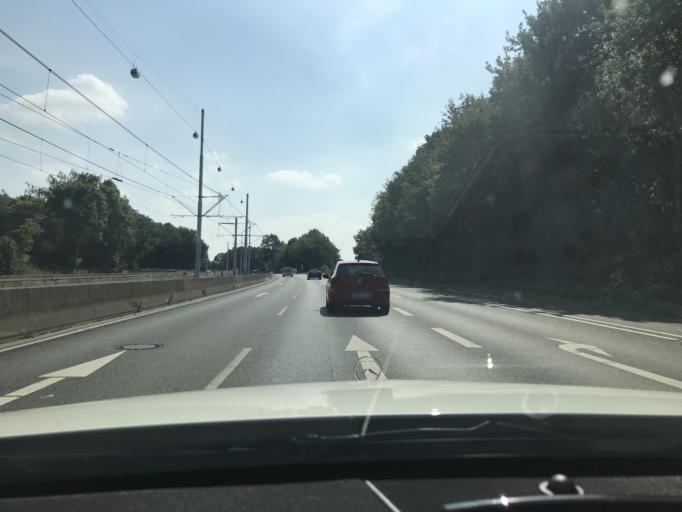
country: DE
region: North Rhine-Westphalia
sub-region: Regierungsbezirk Arnsberg
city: Bochum
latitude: 51.4503
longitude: 7.2477
